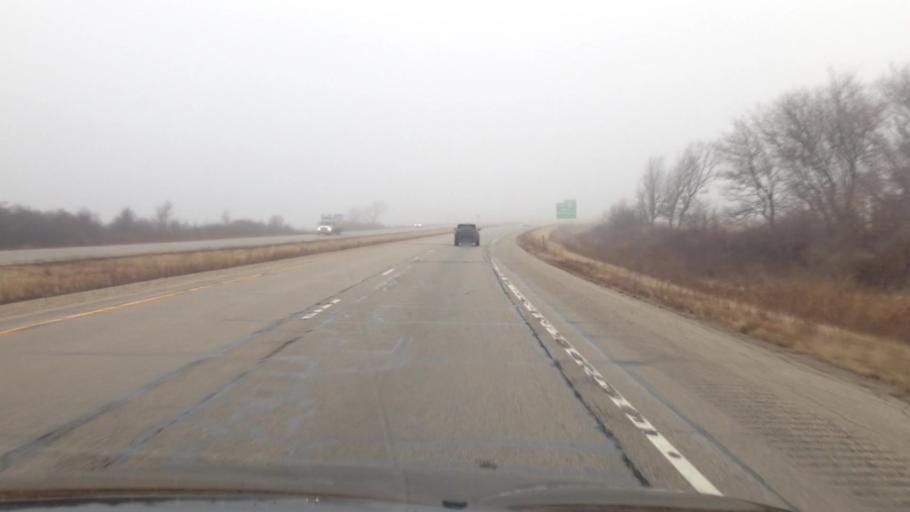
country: US
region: Wisconsin
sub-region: Walworth County
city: Como
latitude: 42.6476
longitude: -88.5034
